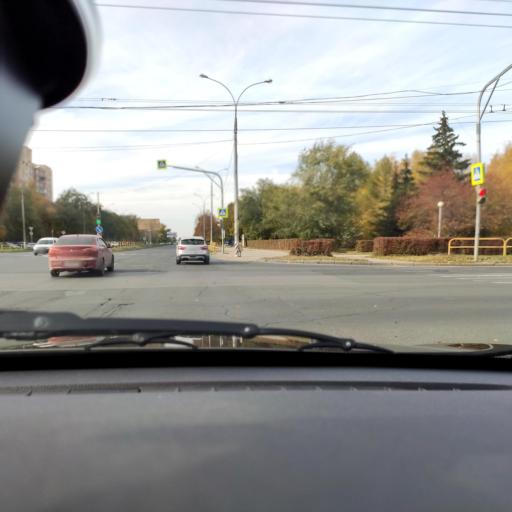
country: RU
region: Samara
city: Tol'yatti
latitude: 53.5155
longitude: 49.2731
